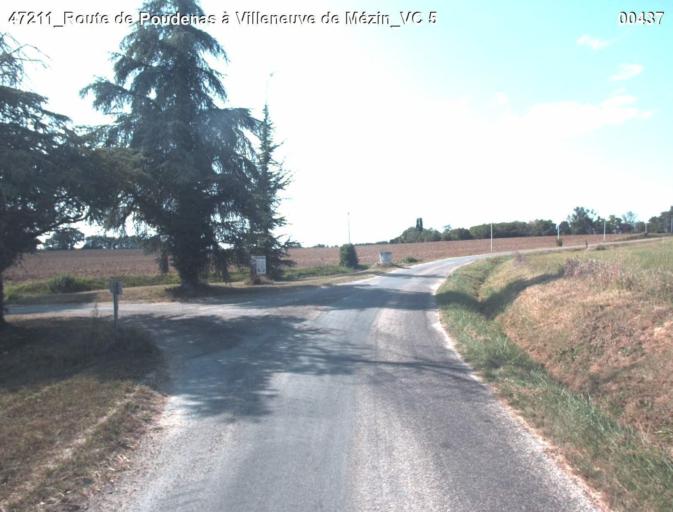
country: FR
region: Aquitaine
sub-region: Departement du Lot-et-Garonne
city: Mezin
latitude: 44.0379
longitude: 0.2196
